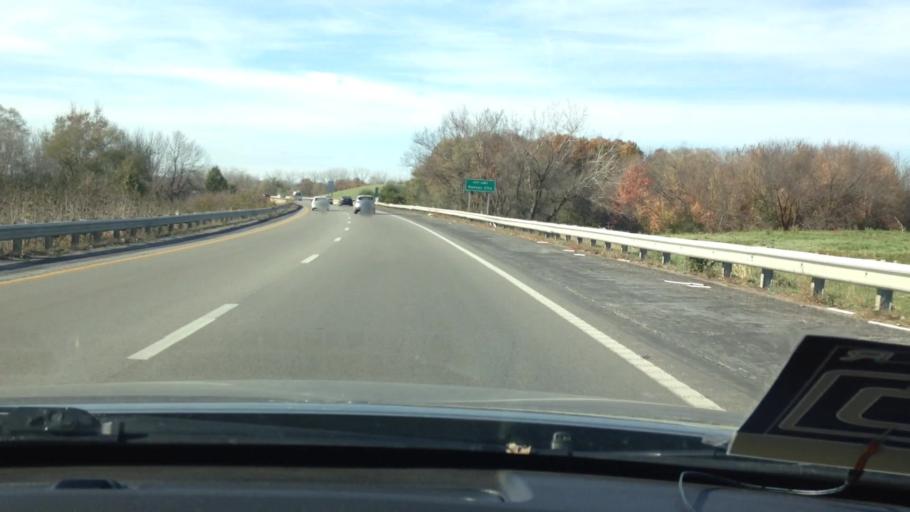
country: US
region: Missouri
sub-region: Platte County
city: Riverside
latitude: 39.1830
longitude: -94.5894
